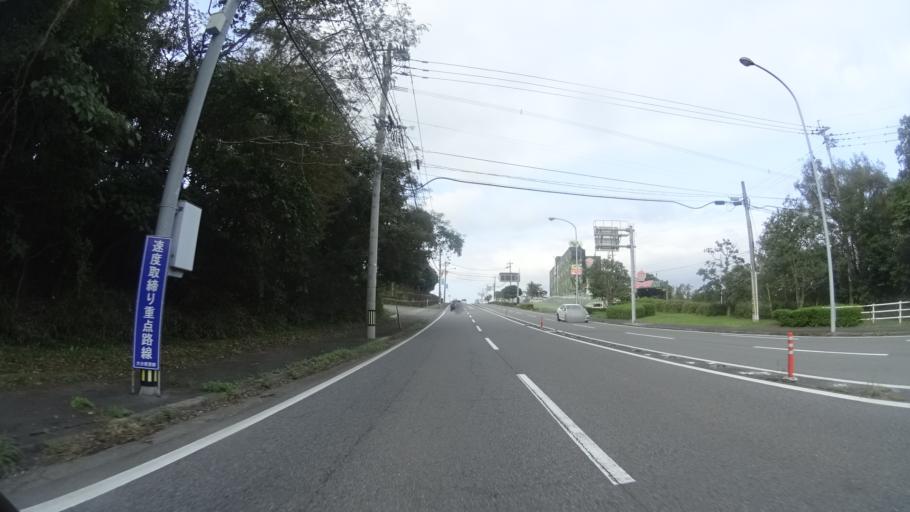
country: JP
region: Oita
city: Beppu
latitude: 33.2935
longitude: 131.4602
